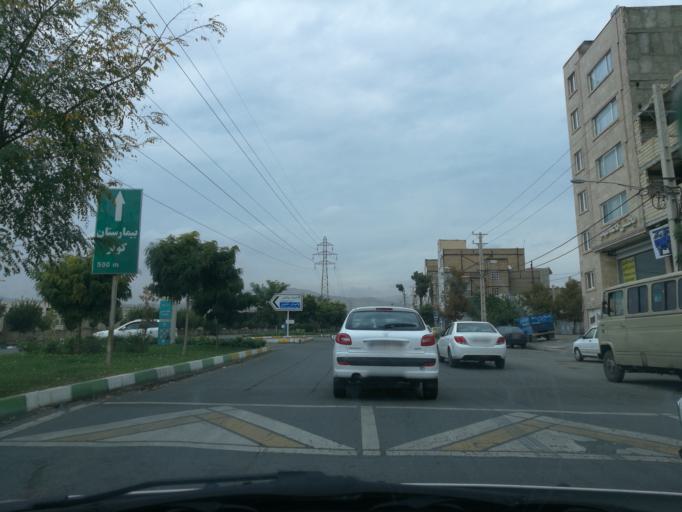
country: IR
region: Alborz
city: Karaj
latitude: 35.8533
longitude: 50.9196
